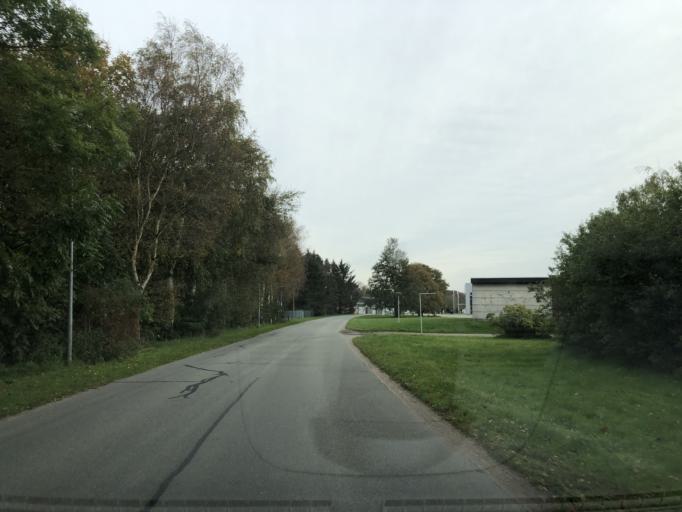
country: DK
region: Central Jutland
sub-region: Syddjurs Kommune
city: Hornslet
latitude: 56.3070
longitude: 10.3120
